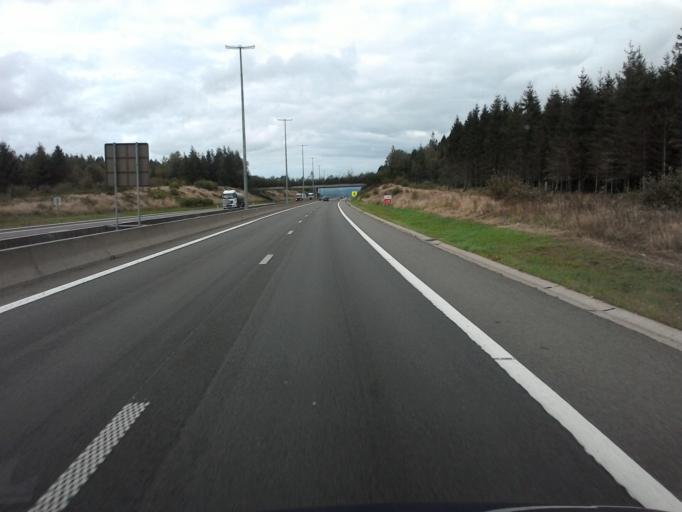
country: BE
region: Wallonia
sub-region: Province du Luxembourg
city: Manhay
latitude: 50.2596
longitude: 5.7252
